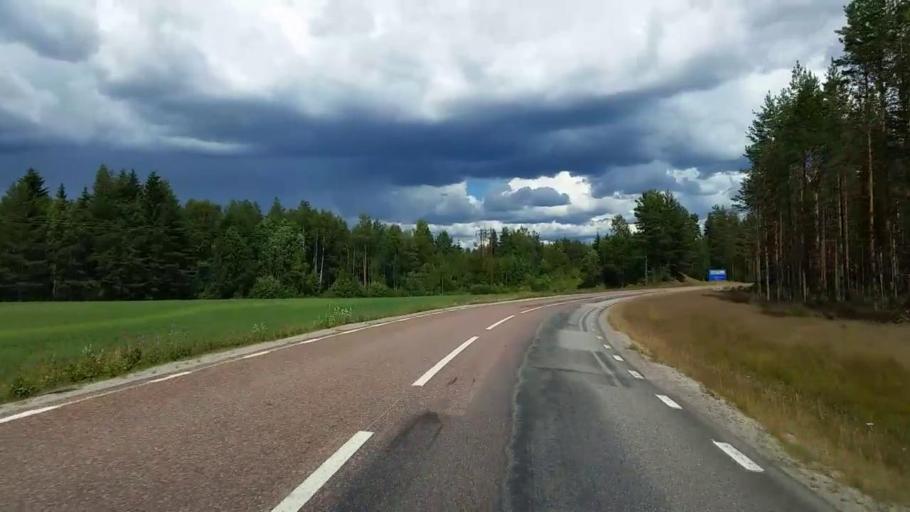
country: SE
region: Gaevleborg
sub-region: Ovanakers Kommun
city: Edsbyn
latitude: 61.3411
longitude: 15.5442
